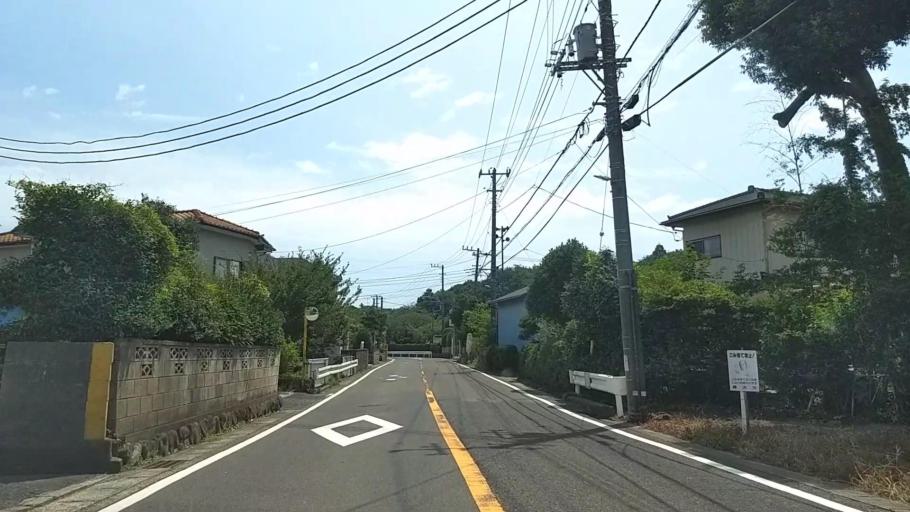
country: JP
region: Kanagawa
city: Minami-rinkan
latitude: 35.4136
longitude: 139.4283
